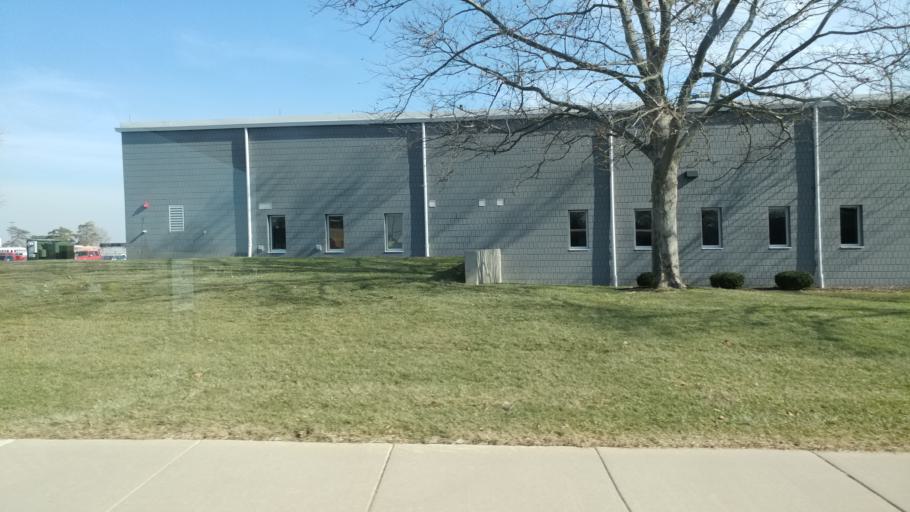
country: US
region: Ohio
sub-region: Wood County
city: Bowling Green
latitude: 41.3835
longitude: -83.6396
